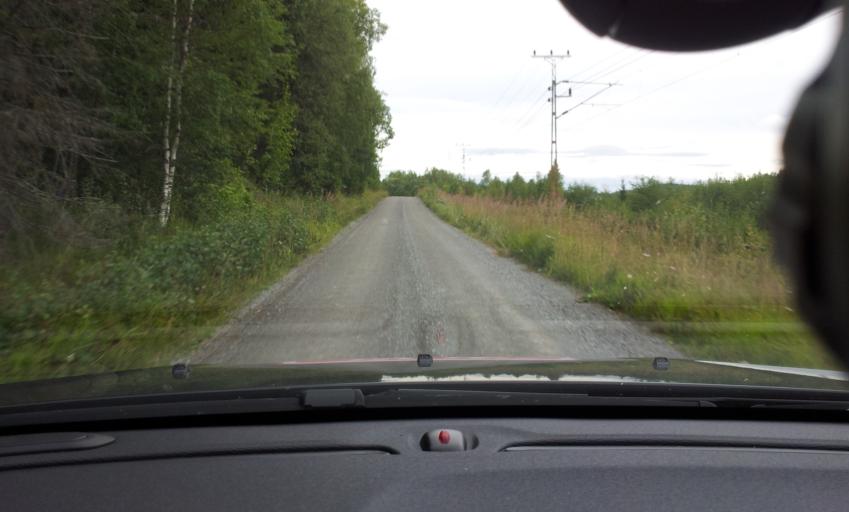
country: SE
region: Jaemtland
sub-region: OEstersunds Kommun
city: Brunflo
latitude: 63.0019
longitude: 14.9550
